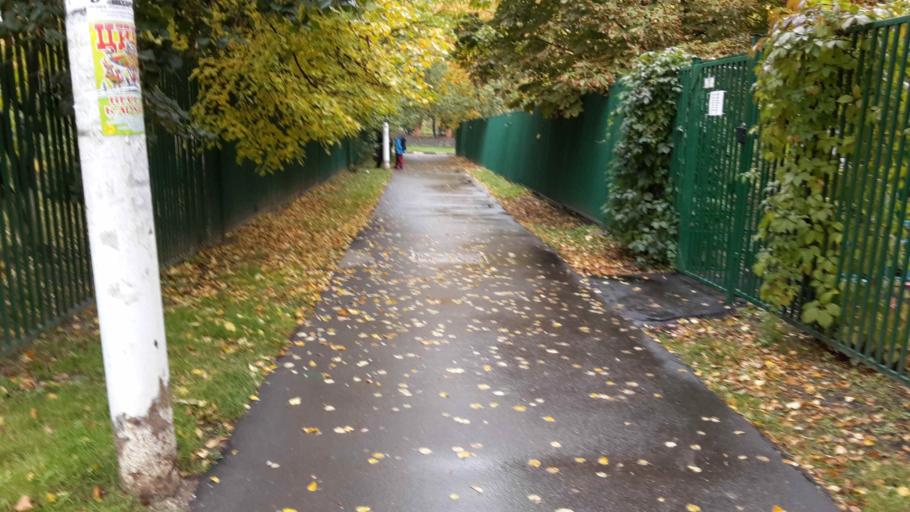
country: RU
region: Moskovskaya
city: Kur'yanovo
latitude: 55.6387
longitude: 37.6994
